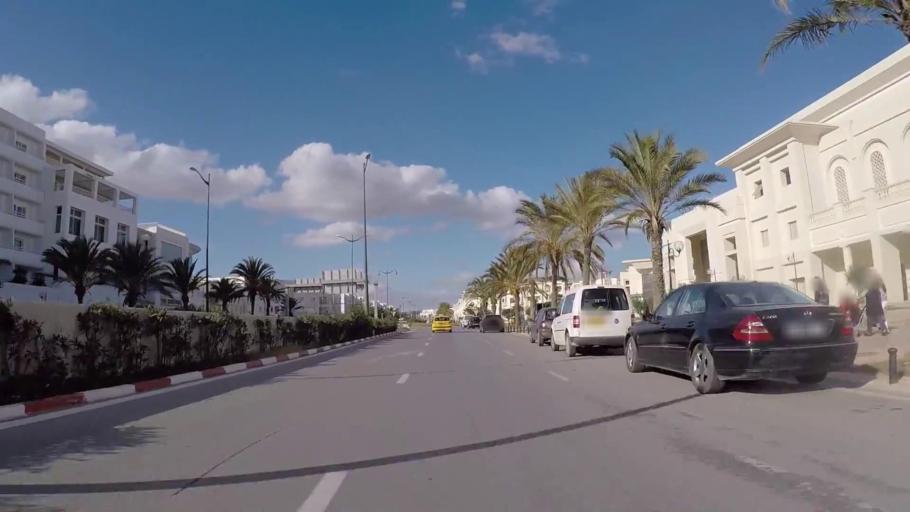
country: TN
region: Nabul
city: Al Hammamat
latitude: 36.3719
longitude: 10.5418
